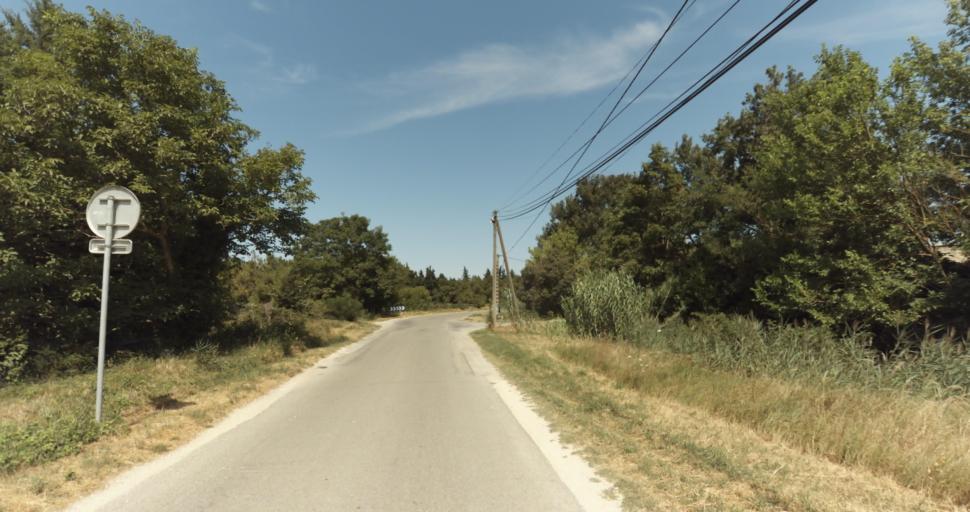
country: FR
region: Provence-Alpes-Cote d'Azur
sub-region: Departement du Vaucluse
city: Althen-des-Paluds
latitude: 44.0197
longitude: 4.9769
